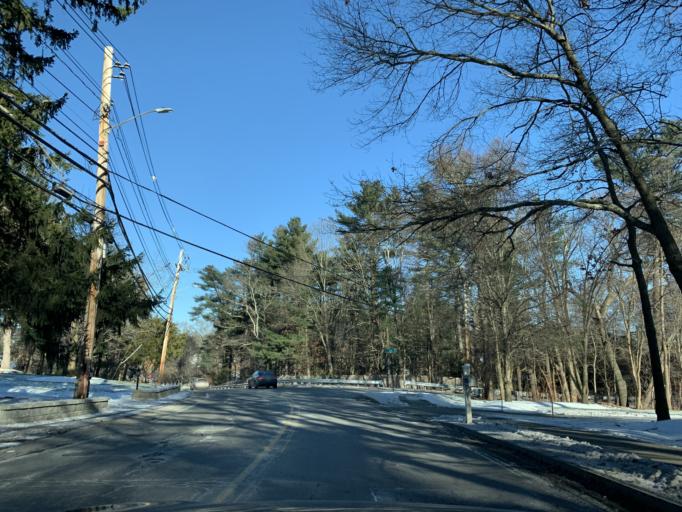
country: US
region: Massachusetts
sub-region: Norfolk County
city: Canton
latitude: 42.1869
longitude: -71.1479
